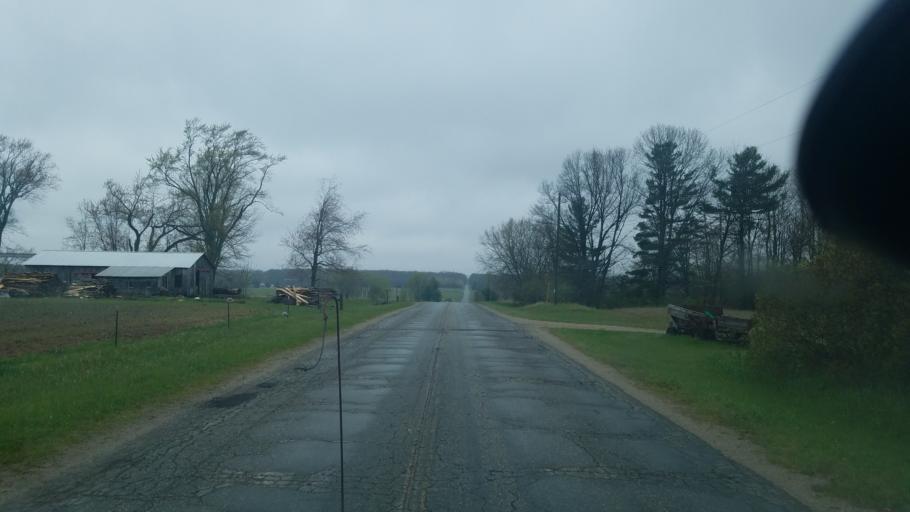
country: US
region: Michigan
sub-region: Mecosta County
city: Canadian Lakes
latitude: 43.5680
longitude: -85.3442
